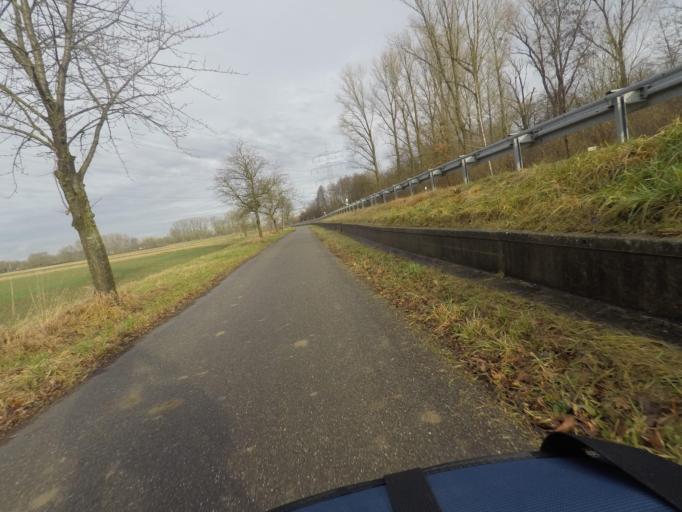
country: DE
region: Baden-Wuerttemberg
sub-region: Karlsruhe Region
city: Steinmauern
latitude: 48.9187
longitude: 8.2045
